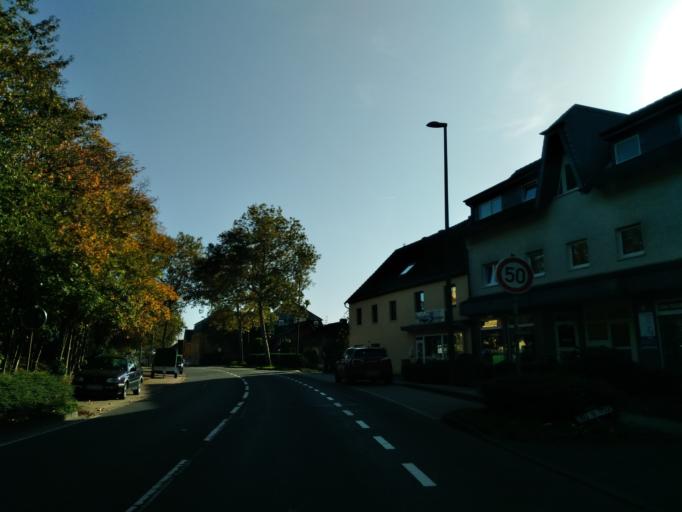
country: DE
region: Rheinland-Pfalz
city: Asbach
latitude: 50.7347
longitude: 7.3653
